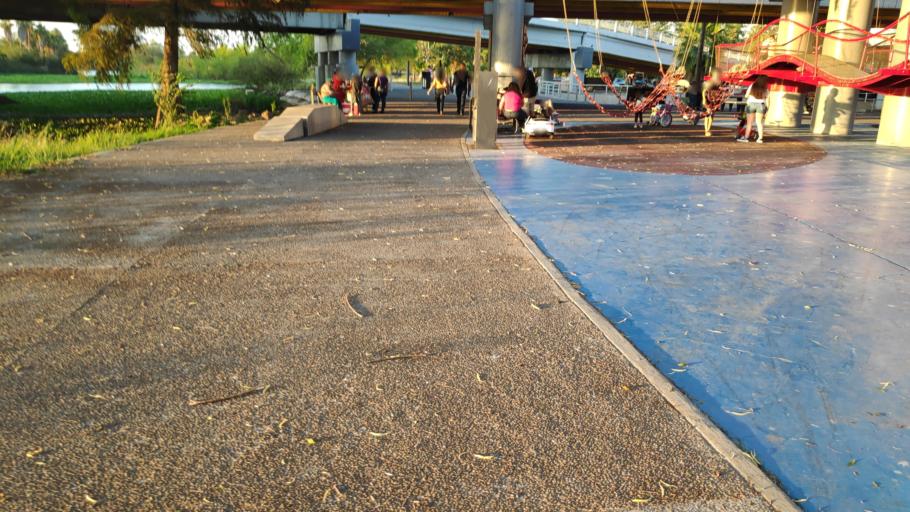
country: MX
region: Sinaloa
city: Culiacan
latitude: 24.8089
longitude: -107.4079
